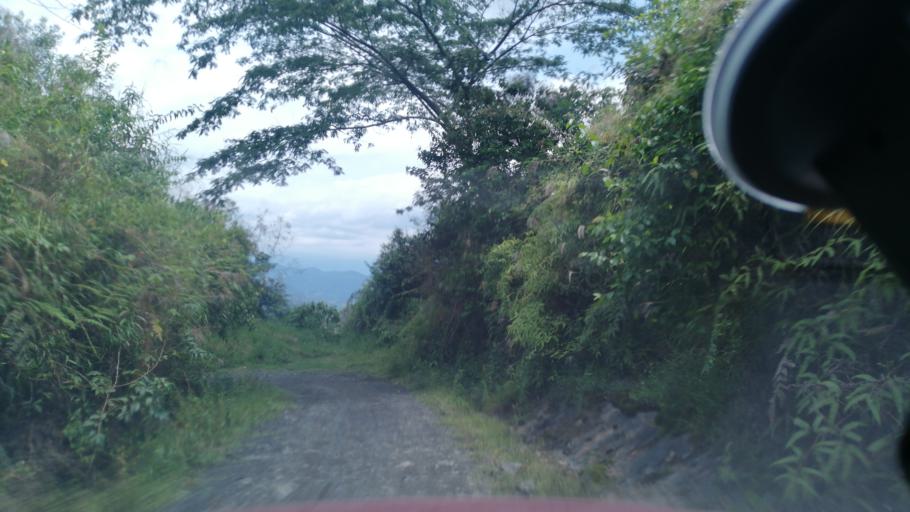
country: CO
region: Cundinamarca
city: Vergara
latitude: 5.1974
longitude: -74.2920
